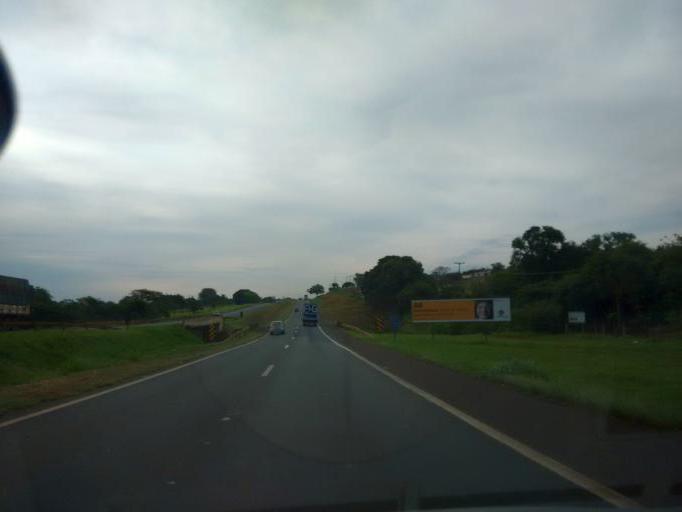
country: BR
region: Sao Paulo
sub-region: Araraquara
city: Araraquara
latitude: -21.7990
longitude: -48.2052
